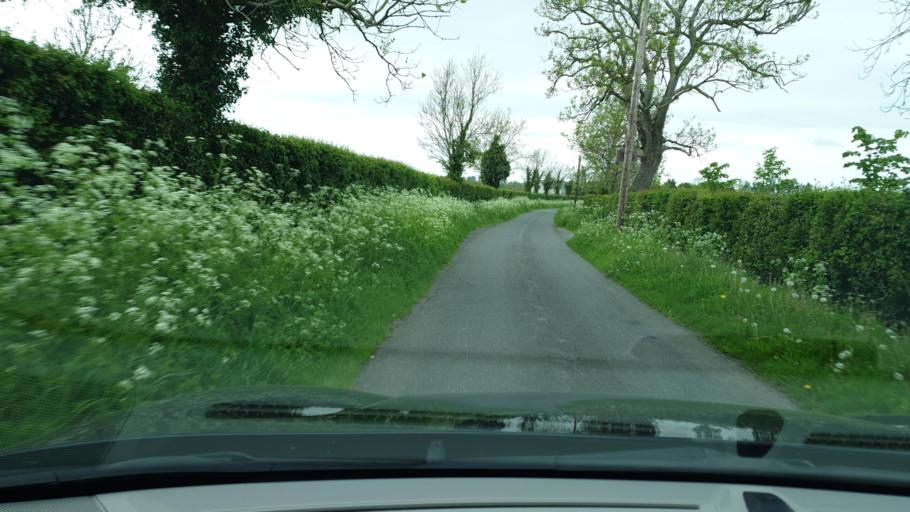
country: IE
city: Confey
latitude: 53.4137
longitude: -6.5294
